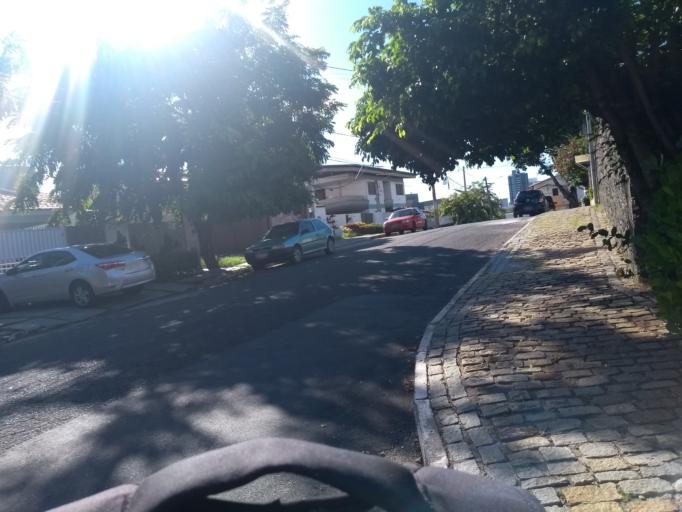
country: BR
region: Bahia
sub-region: Salvador
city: Salvador
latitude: -12.9958
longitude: -38.4611
